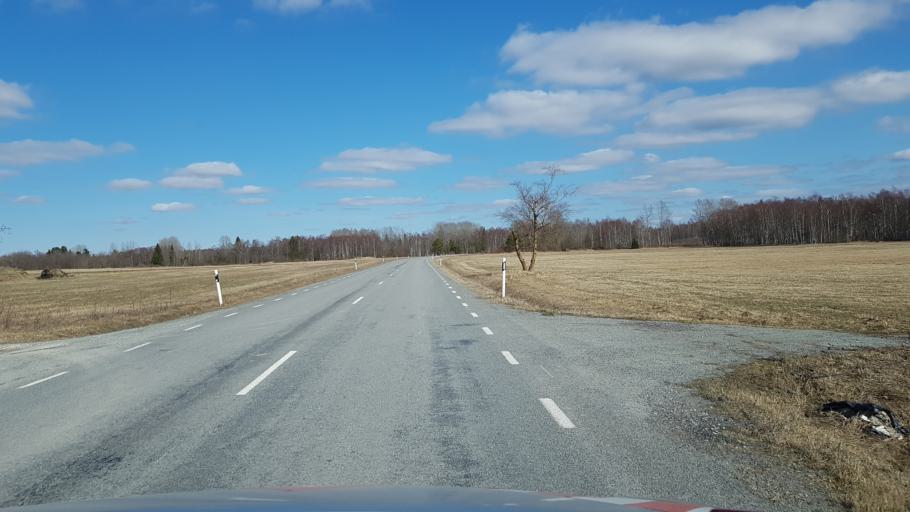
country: EE
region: Laeaene-Virumaa
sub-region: Tapa vald
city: Tapa
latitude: 59.2764
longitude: 25.8756
